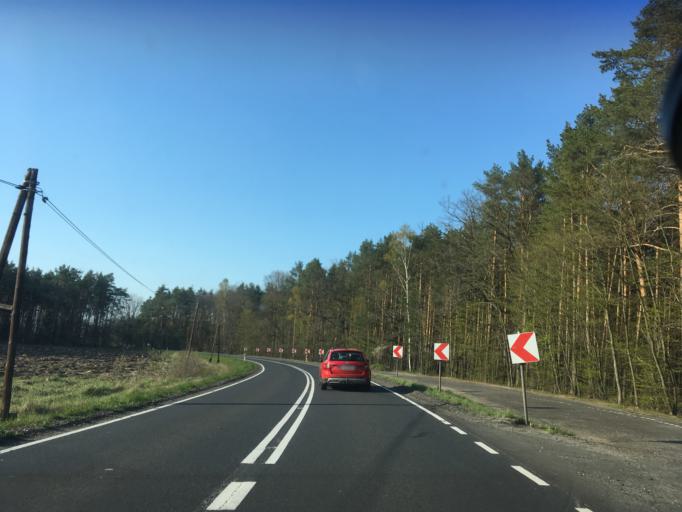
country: PL
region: Lubusz
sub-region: Powiat zaganski
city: Szprotawa
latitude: 51.4977
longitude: 15.6246
